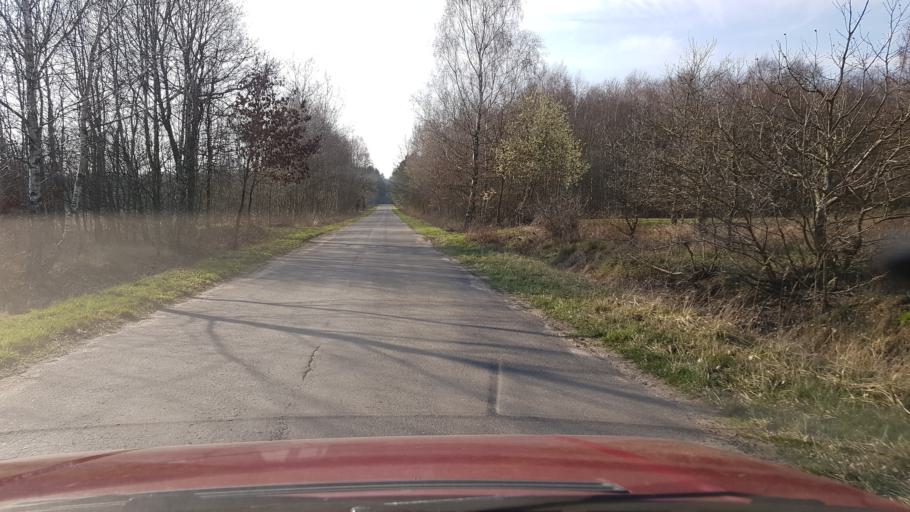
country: PL
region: West Pomeranian Voivodeship
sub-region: Powiat gryficki
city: Ploty
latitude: 53.8296
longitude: 15.3290
